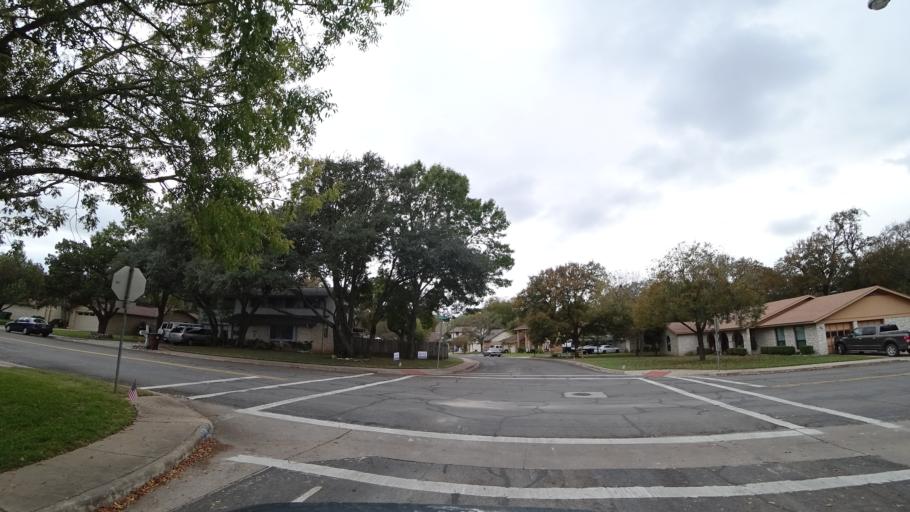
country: US
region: Texas
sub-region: Williamson County
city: Round Rock
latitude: 30.4971
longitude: -97.7024
